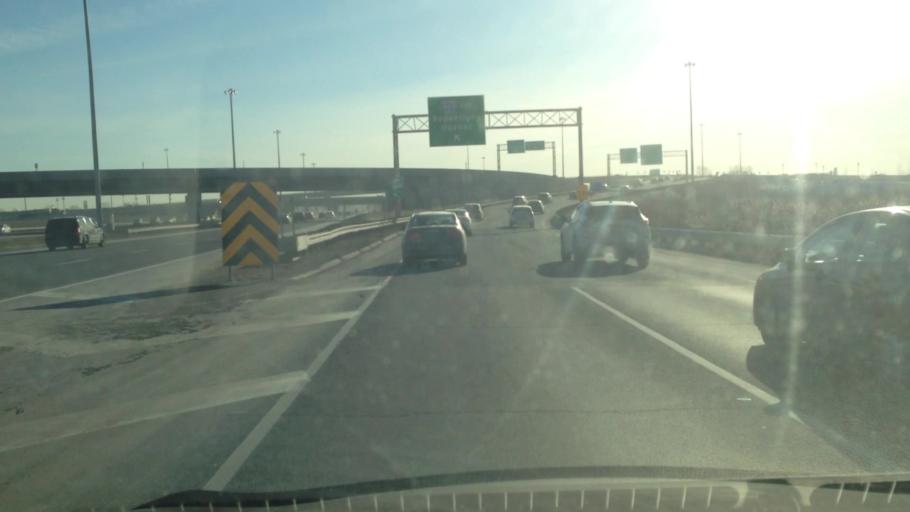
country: CA
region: Quebec
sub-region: Laurentides
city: Boisbriand
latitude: 45.6303
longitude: -73.8453
